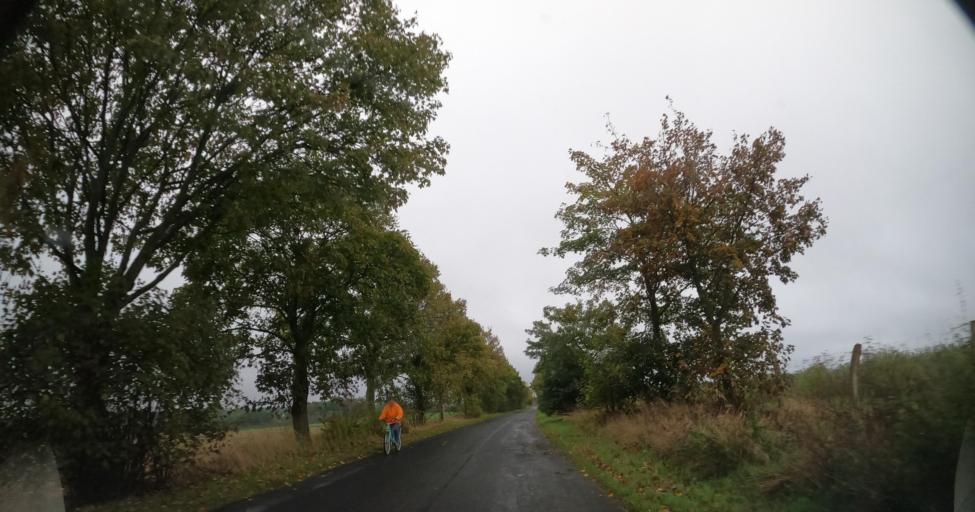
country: PL
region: West Pomeranian Voivodeship
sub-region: Powiat pyrzycki
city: Kozielice
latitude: 53.0768
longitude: 14.7833
